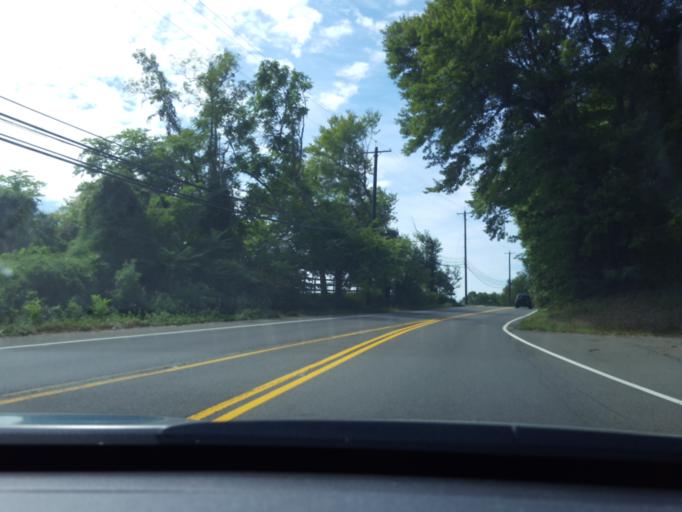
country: US
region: Maryland
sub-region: Prince George's County
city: Mellwood
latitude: 38.8000
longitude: -76.8267
